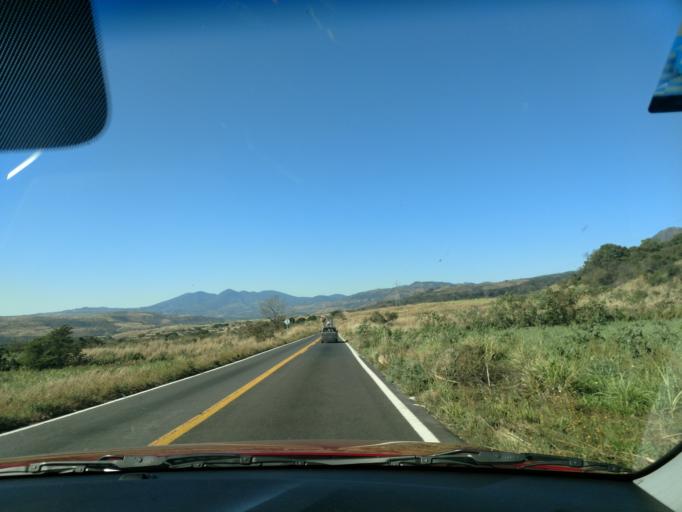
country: MX
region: Nayarit
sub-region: Ahuacatlan
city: Ahuacatlan
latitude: 21.1149
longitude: -104.5902
